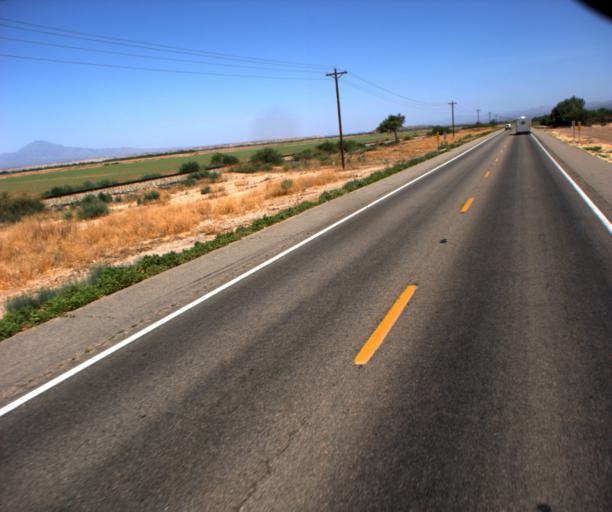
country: US
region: Arizona
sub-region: Graham County
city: Pima
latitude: 32.9661
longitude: -109.9227
